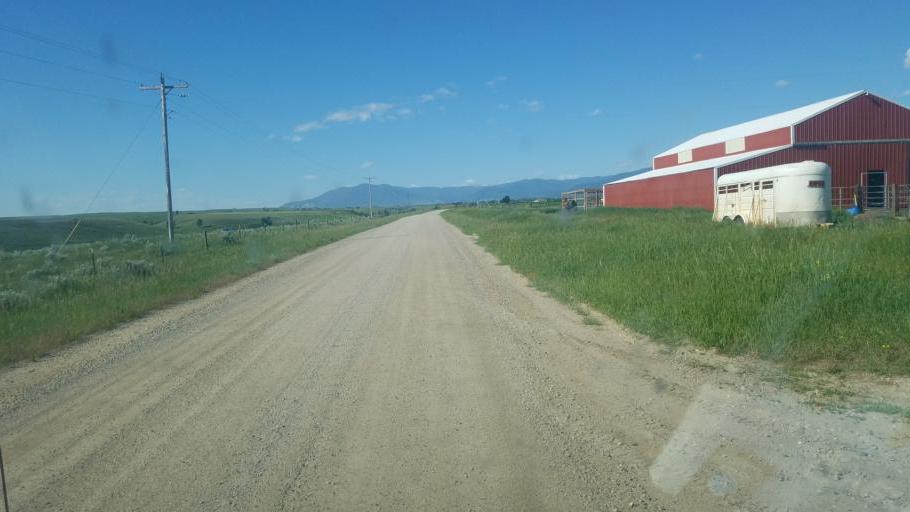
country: US
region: Montana
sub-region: Carbon County
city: Red Lodge
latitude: 45.3363
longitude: -109.1627
